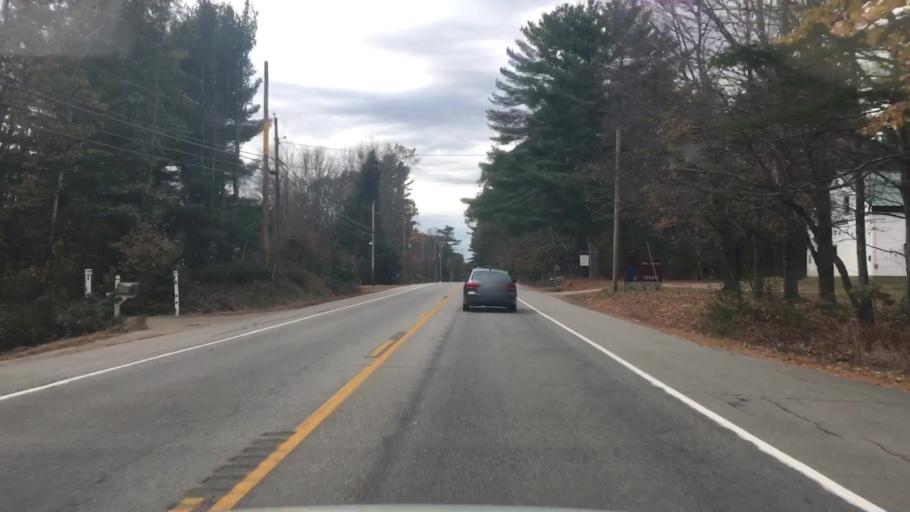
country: US
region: Maine
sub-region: York County
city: Alfred
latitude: 43.4764
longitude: -70.6786
